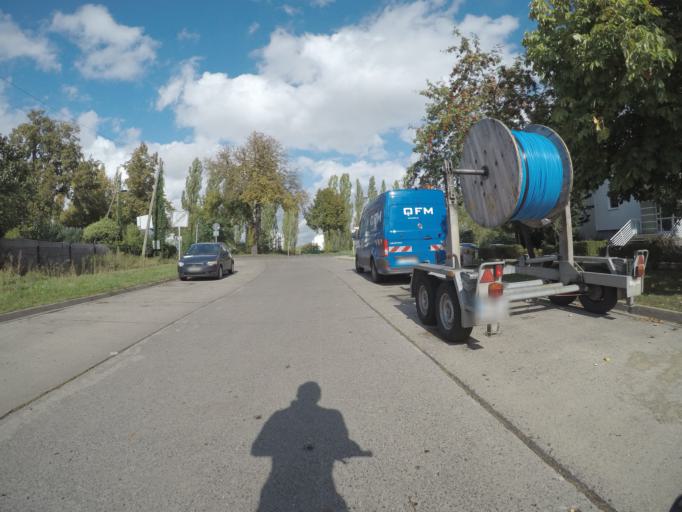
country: DE
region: Berlin
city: Falkenberg
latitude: 52.5711
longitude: 13.5608
